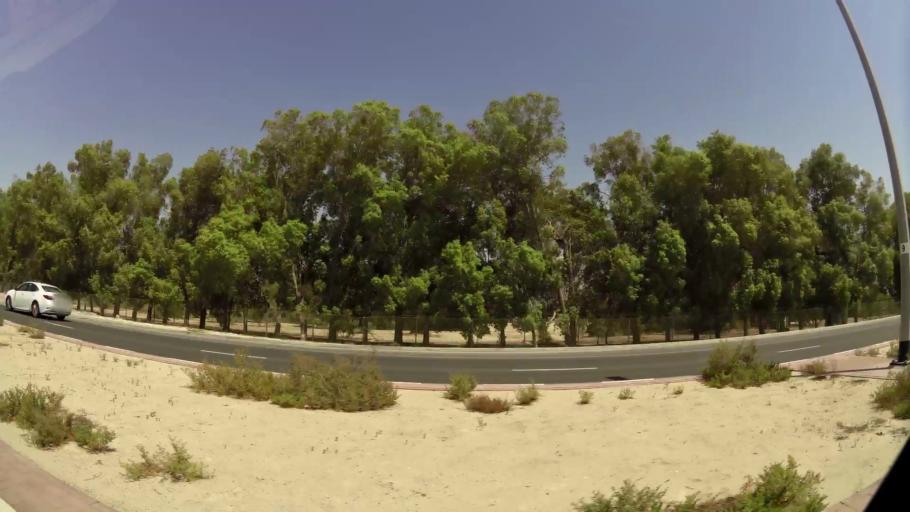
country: AE
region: Dubai
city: Dubai
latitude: 25.1273
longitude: 55.1886
